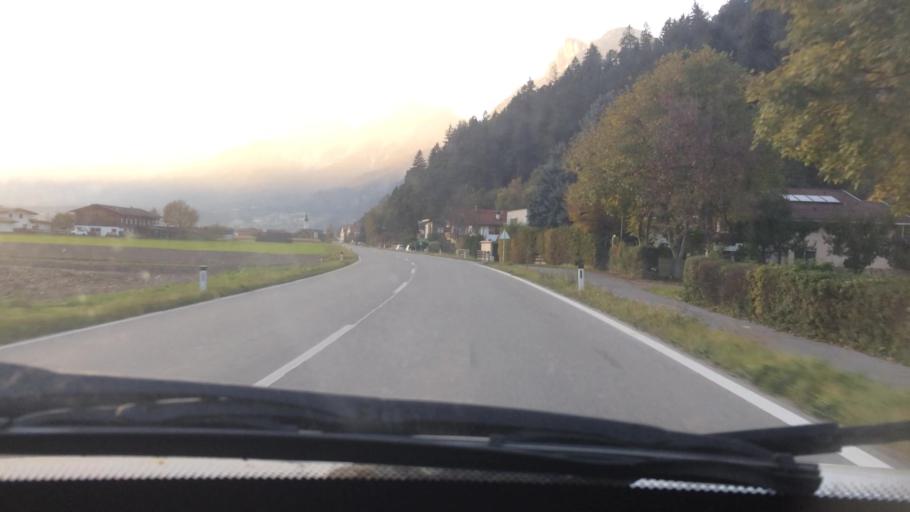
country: AT
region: Tyrol
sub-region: Politischer Bezirk Innsbruck Land
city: Polling in Tirol
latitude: 47.2958
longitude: 11.1504
